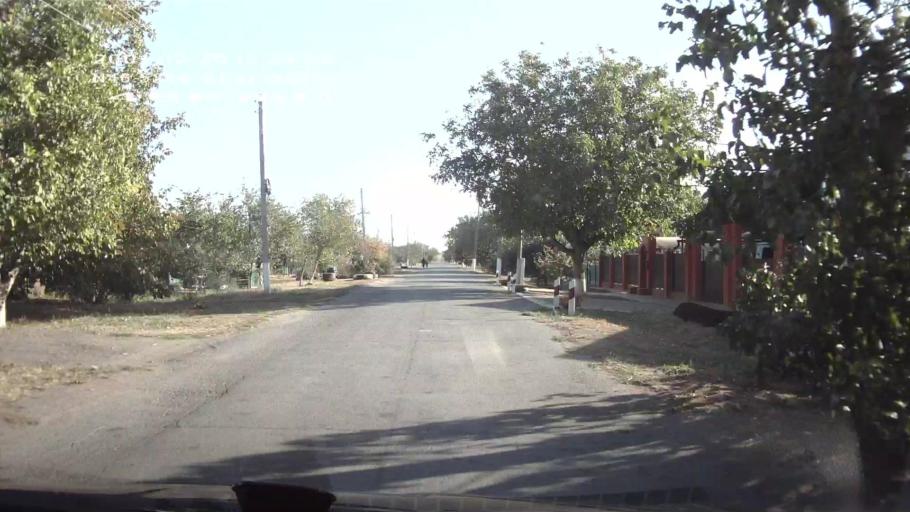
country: RU
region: Rostov
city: Gigant
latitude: 46.5262
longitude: 41.1900
